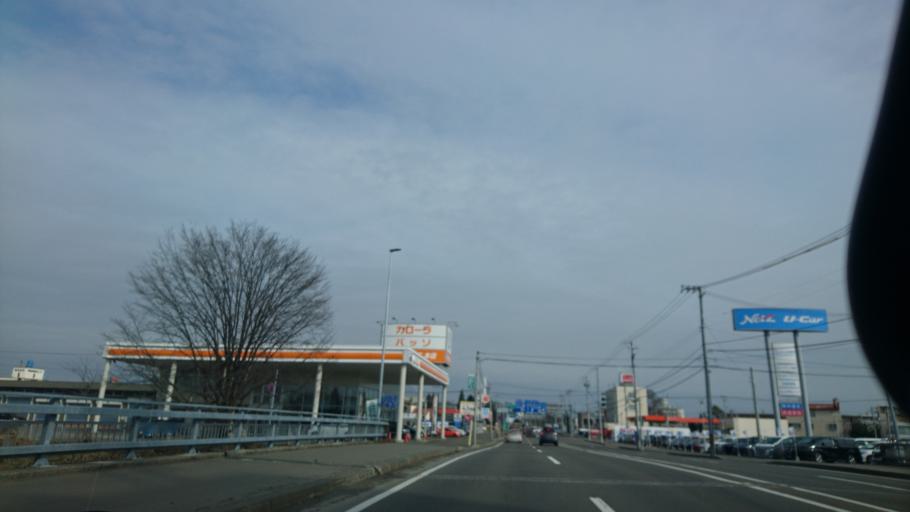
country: JP
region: Hokkaido
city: Obihiro
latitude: 42.9300
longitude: 143.2042
